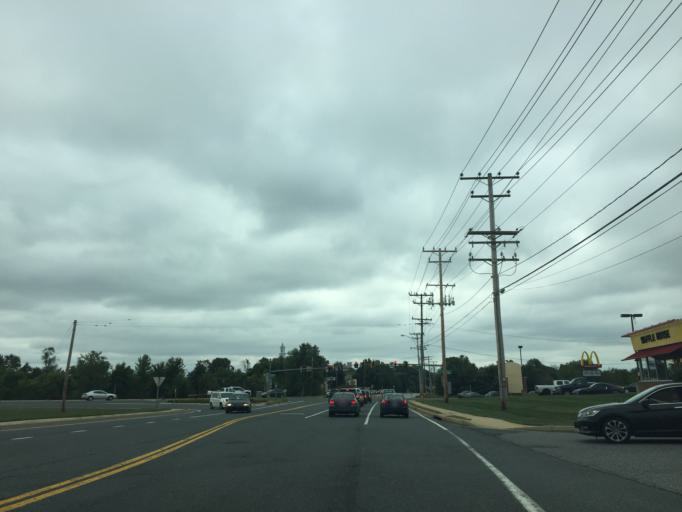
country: US
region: Maryland
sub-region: Harford County
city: Bel Air North
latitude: 39.5680
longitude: -76.3540
